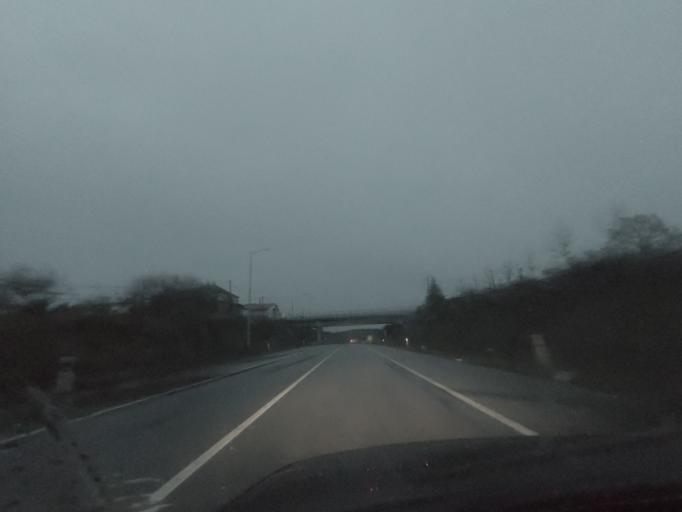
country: PT
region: Vila Real
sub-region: Vila Real
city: Vila Real
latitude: 41.2804
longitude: -7.7031
